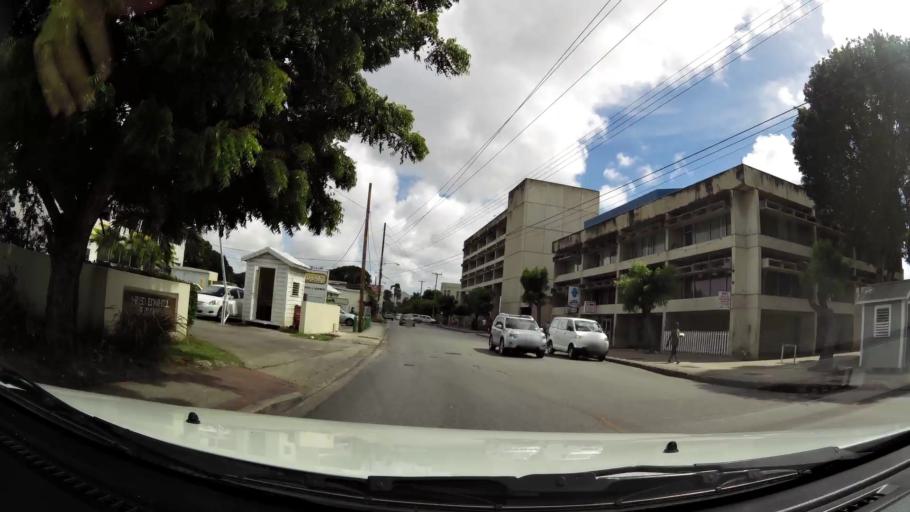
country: BB
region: Saint Michael
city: Bridgetown
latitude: 13.0986
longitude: -59.6212
